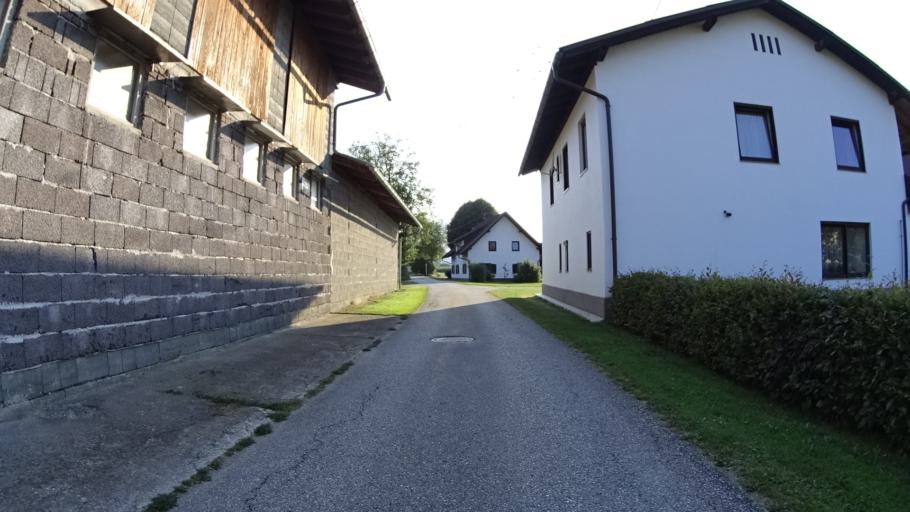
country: AT
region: Carinthia
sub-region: Politischer Bezirk Villach Land
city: Sankt Jakob
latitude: 46.5671
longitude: 14.0581
